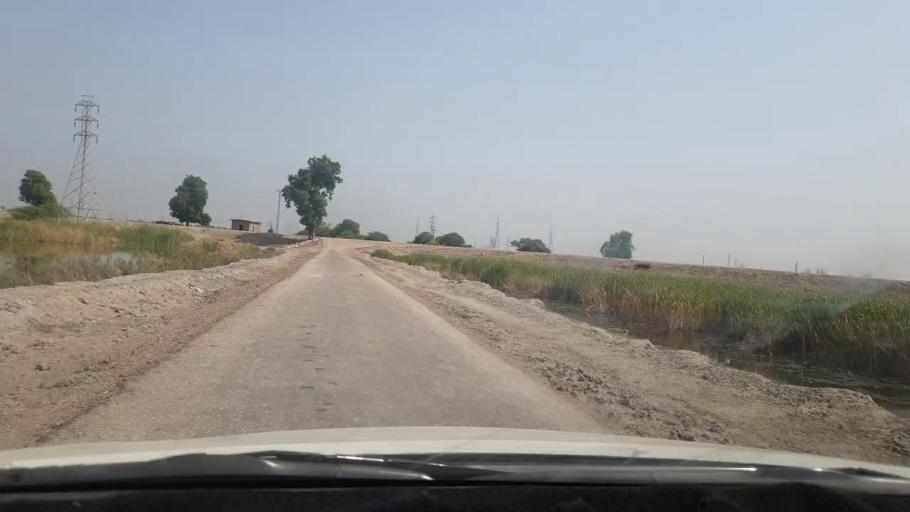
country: PK
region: Sindh
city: Rohri
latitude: 27.6371
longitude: 68.8841
